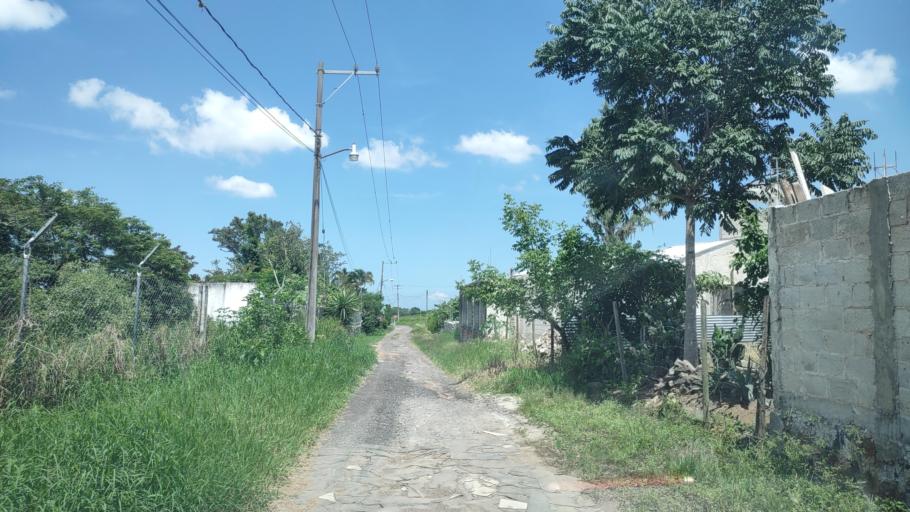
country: MX
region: Veracruz
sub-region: Emiliano Zapata
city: Dos Rios
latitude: 19.4949
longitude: -96.8063
